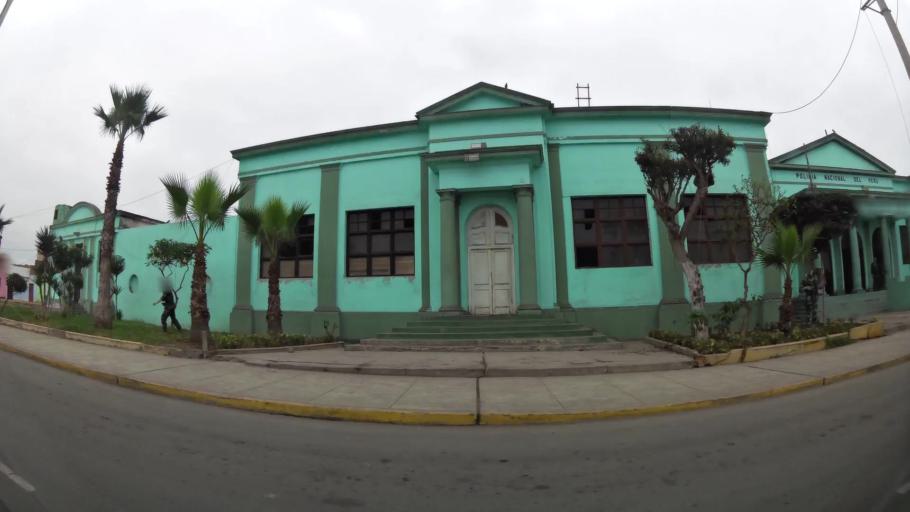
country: PE
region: Callao
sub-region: Callao
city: Callao
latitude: -12.0684
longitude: -77.1334
